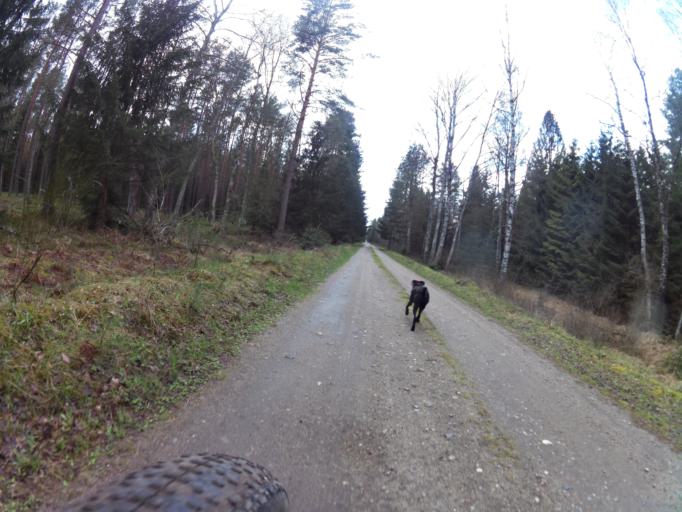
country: PL
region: West Pomeranian Voivodeship
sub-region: Powiat slawienski
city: Slawno
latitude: 54.3186
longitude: 16.7875
